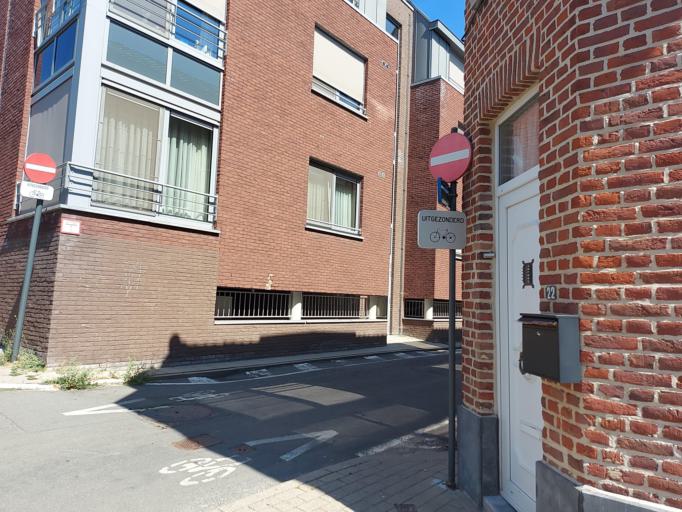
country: BE
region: Flanders
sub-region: Provincie Limburg
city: Tongeren
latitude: 50.7789
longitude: 5.4658
